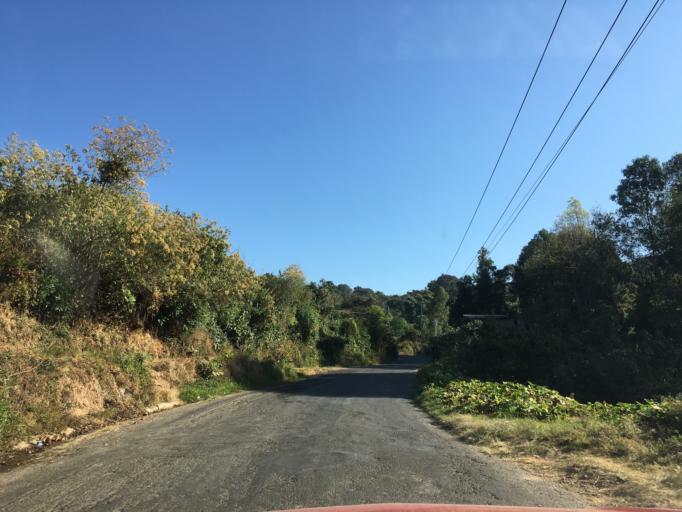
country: MX
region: Michoacan
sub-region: Zitacuaro
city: Valle Verde
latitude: 19.4791
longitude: -100.3343
